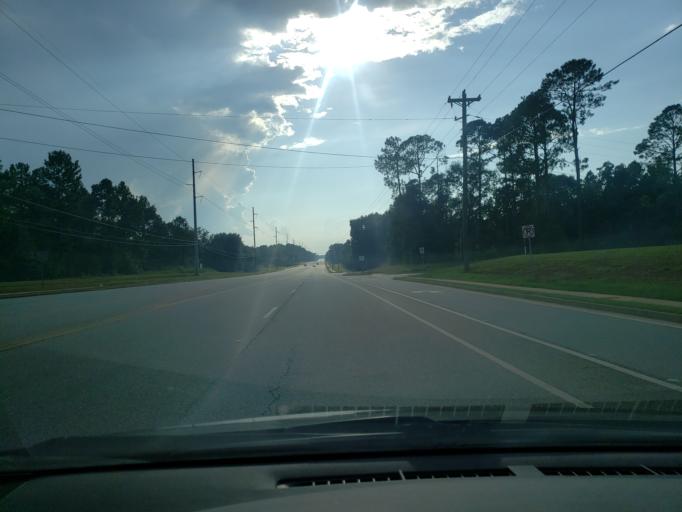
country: US
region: Georgia
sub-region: Dougherty County
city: Albany
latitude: 31.5858
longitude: -84.2520
